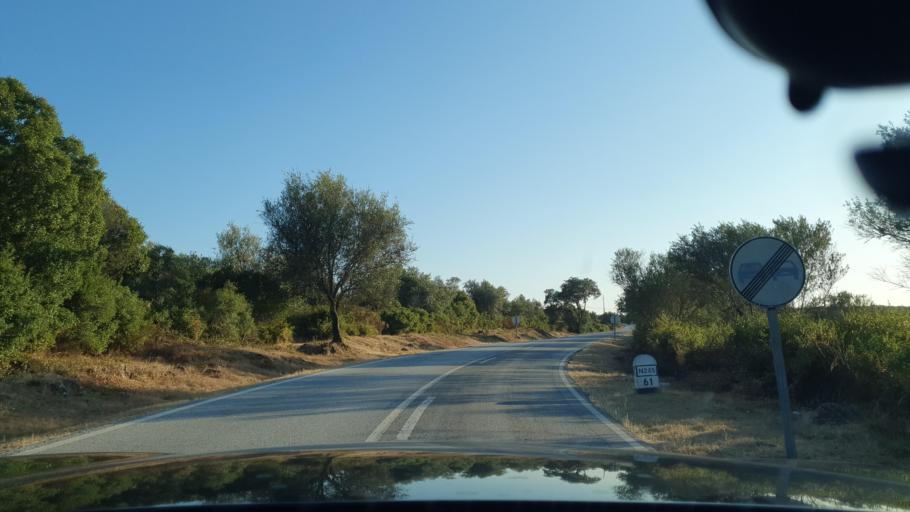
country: PT
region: Evora
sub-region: Estremoz
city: Estremoz
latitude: 38.9179
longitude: -7.6636
